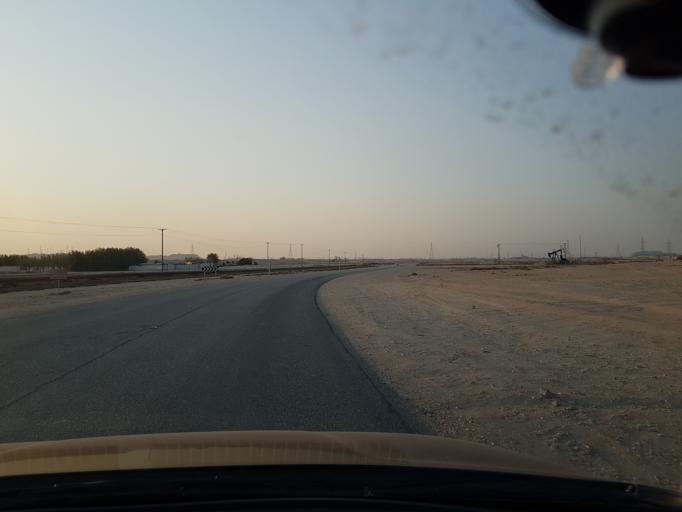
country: BH
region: Central Governorate
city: Dar Kulayb
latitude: 26.0075
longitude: 50.5815
